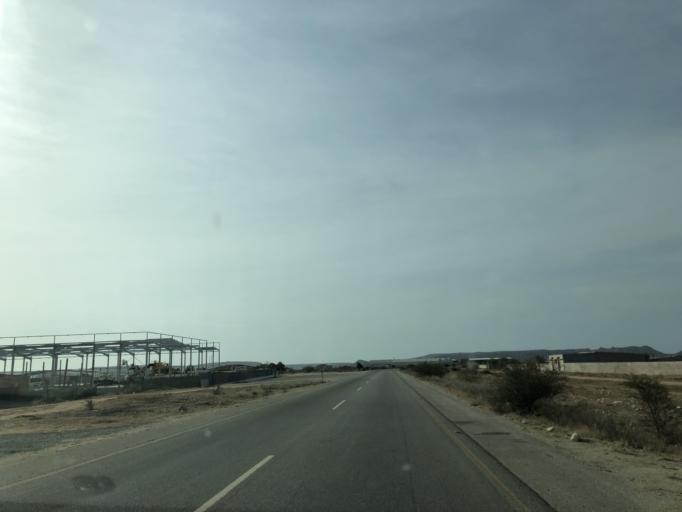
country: AO
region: Benguela
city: Benguela
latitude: -12.6920
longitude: 13.3441
